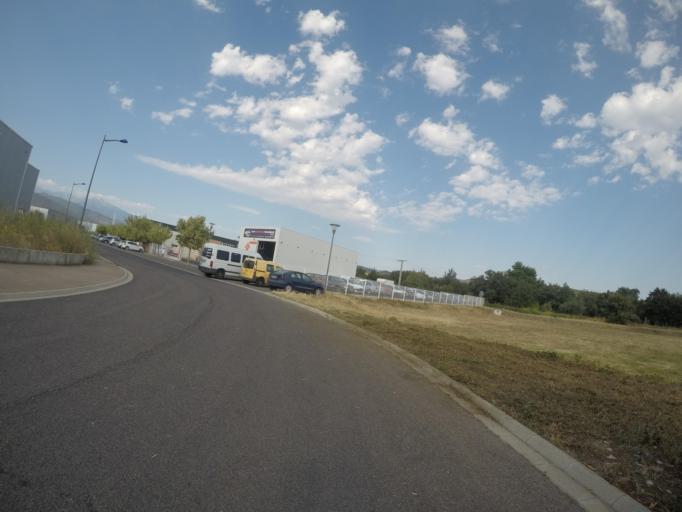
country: FR
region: Languedoc-Roussillon
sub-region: Departement des Pyrenees-Orientales
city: Ille-sur-Tet
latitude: 42.6790
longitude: 2.6362
